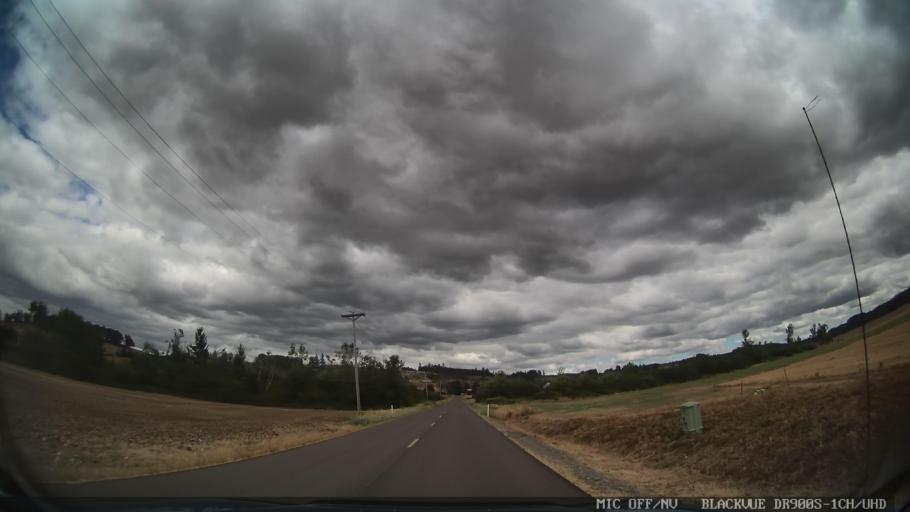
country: US
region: Oregon
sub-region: Marion County
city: Sublimity
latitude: 44.8725
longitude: -122.7177
